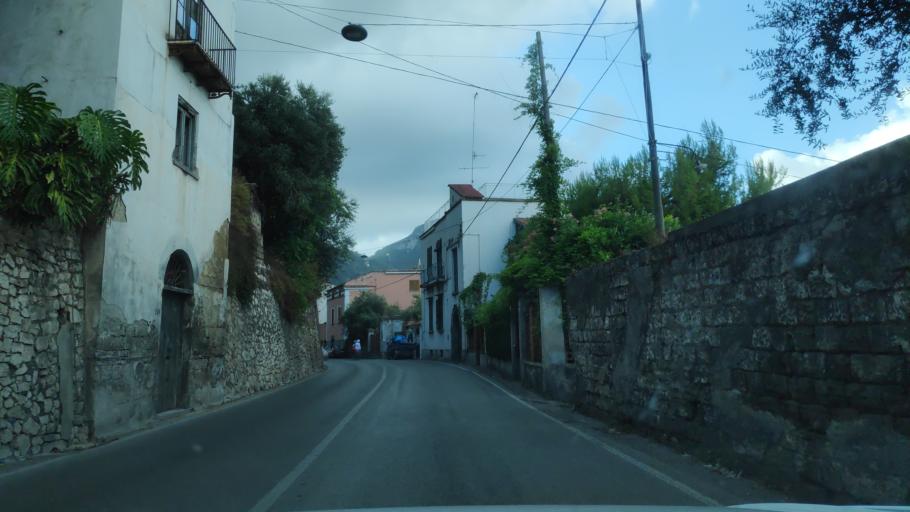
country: IT
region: Campania
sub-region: Provincia di Napoli
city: Meta
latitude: 40.6441
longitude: 14.4157
